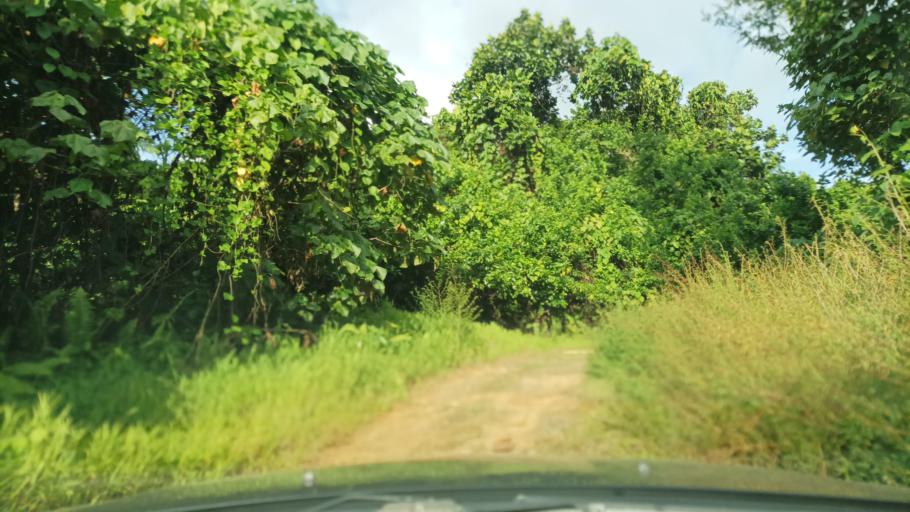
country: FM
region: Kosrae
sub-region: Utwe Municipality
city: Utwe
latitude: 5.2762
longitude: 162.9384
